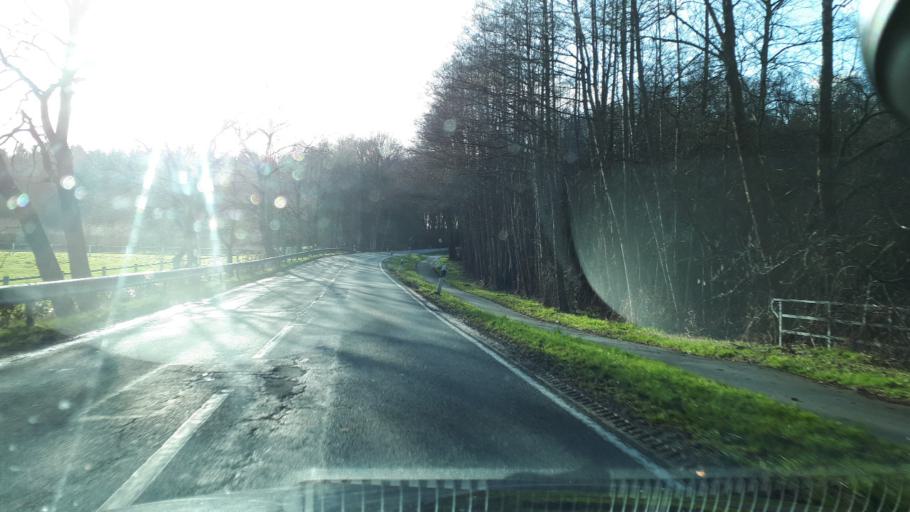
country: DE
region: Lower Saxony
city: Molbergen
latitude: 52.8512
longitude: 7.9735
